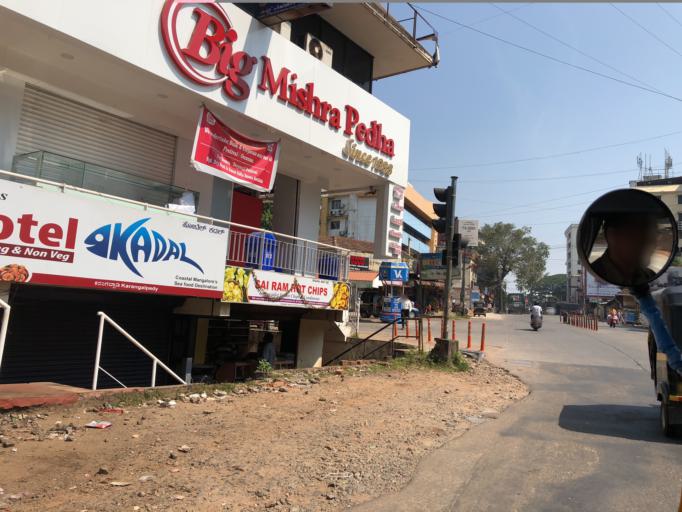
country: IN
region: Karnataka
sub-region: Dakshina Kannada
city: Mangalore
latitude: 12.8760
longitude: 74.8466
